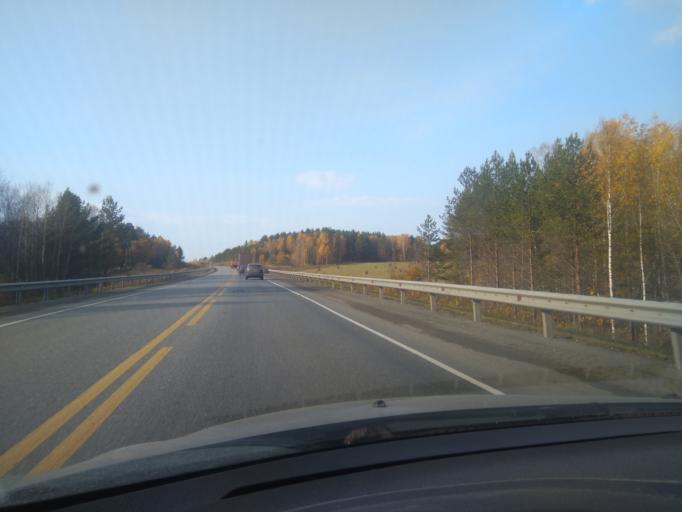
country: RU
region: Sverdlovsk
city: Druzhinino
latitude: 56.8089
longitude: 59.4967
